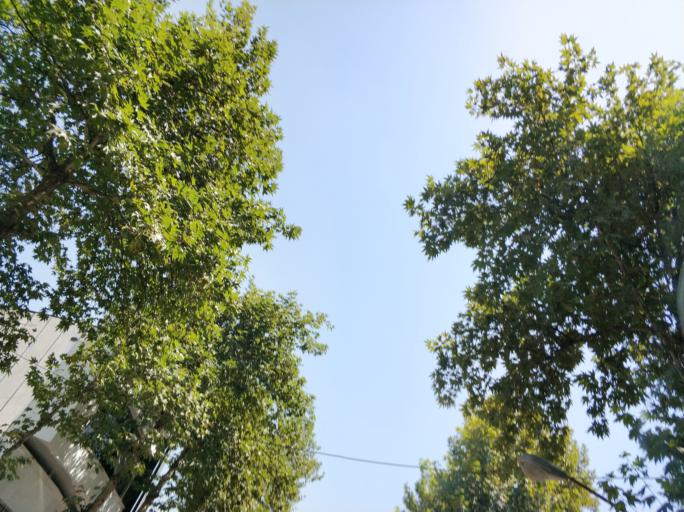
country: IR
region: Gilan
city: Lahijan
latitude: 37.1978
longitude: 50.0126
